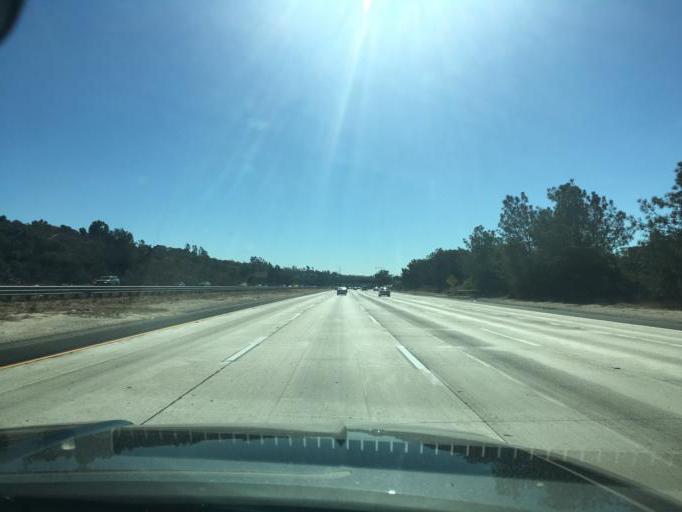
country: US
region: California
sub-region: San Diego County
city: La Mesa
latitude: 32.8162
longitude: -117.1152
